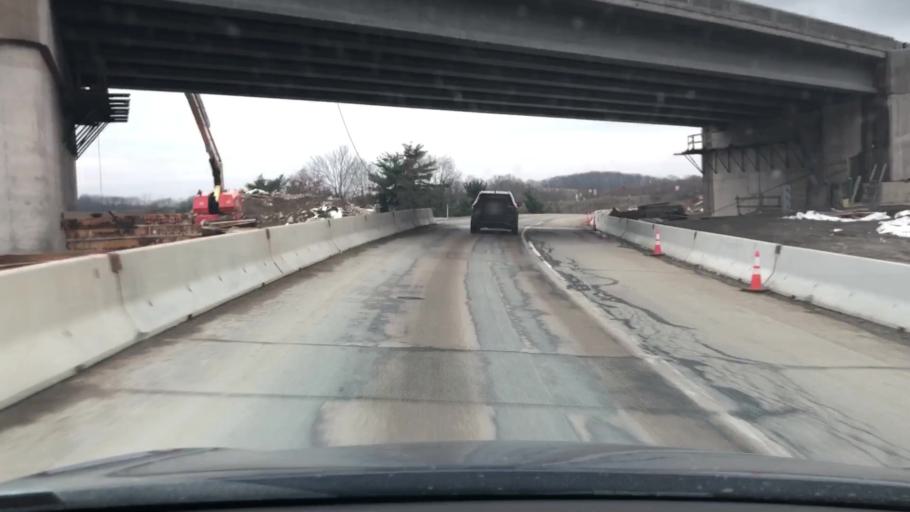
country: US
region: Pennsylvania
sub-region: Armstrong County
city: West Hills
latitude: 40.8093
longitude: -79.5479
